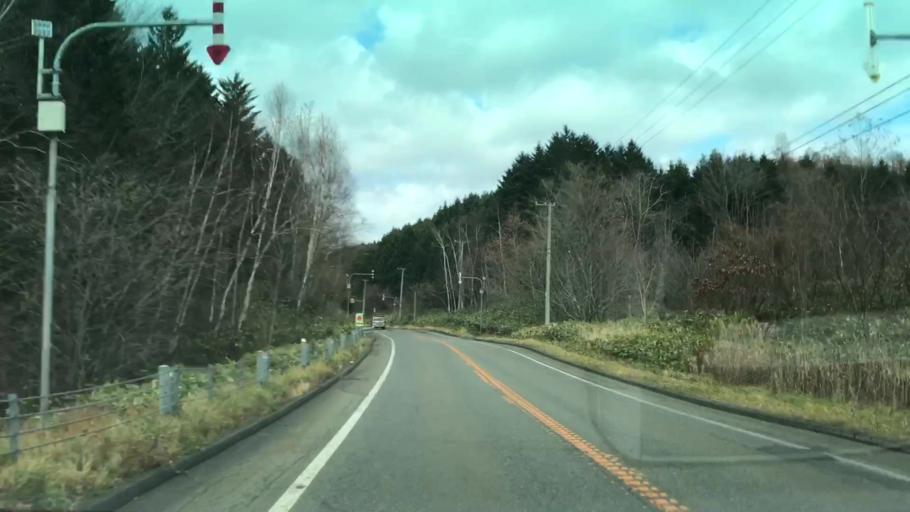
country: JP
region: Hokkaido
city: Shimo-furano
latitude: 42.8940
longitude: 142.4358
